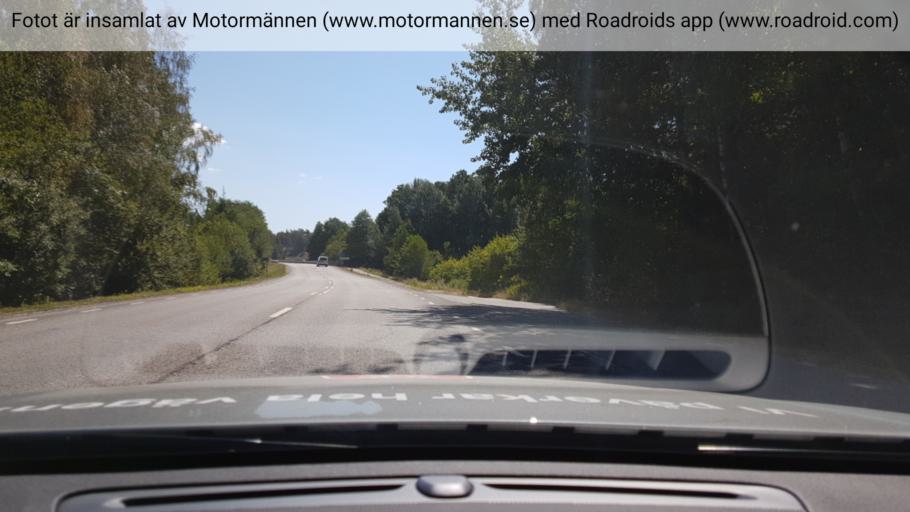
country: SE
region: Stockholm
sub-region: Ekero Kommun
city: Ekeroe
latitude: 59.3066
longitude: 17.7783
